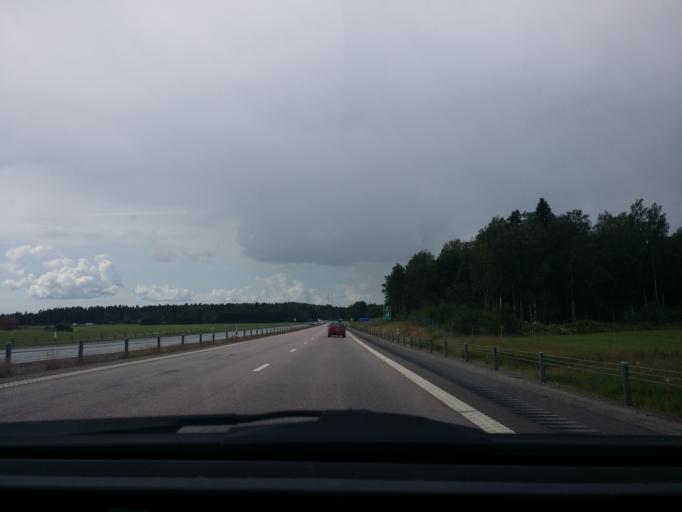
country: SE
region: Vaestmanland
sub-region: Hallstahammars Kommun
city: Kolback
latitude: 59.5841
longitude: 16.3710
